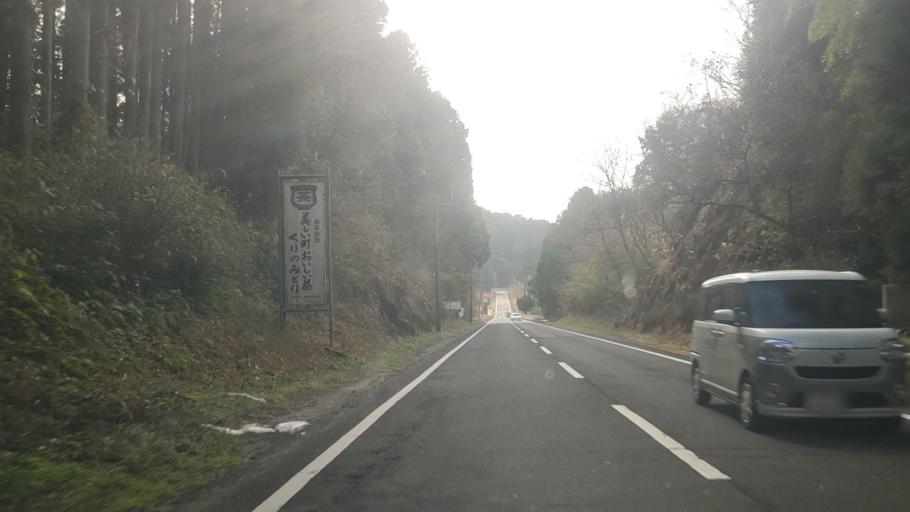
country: JP
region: Kagoshima
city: Okuchi-shinohara
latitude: 31.9664
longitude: 130.7393
